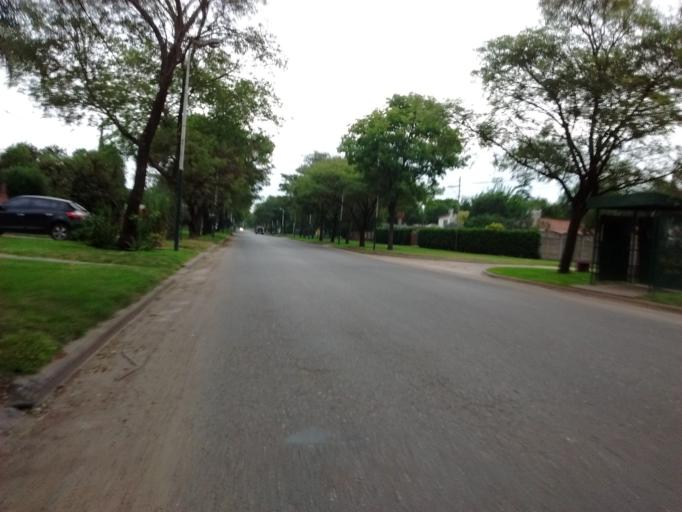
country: AR
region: Santa Fe
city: Funes
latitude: -32.9247
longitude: -60.8116
